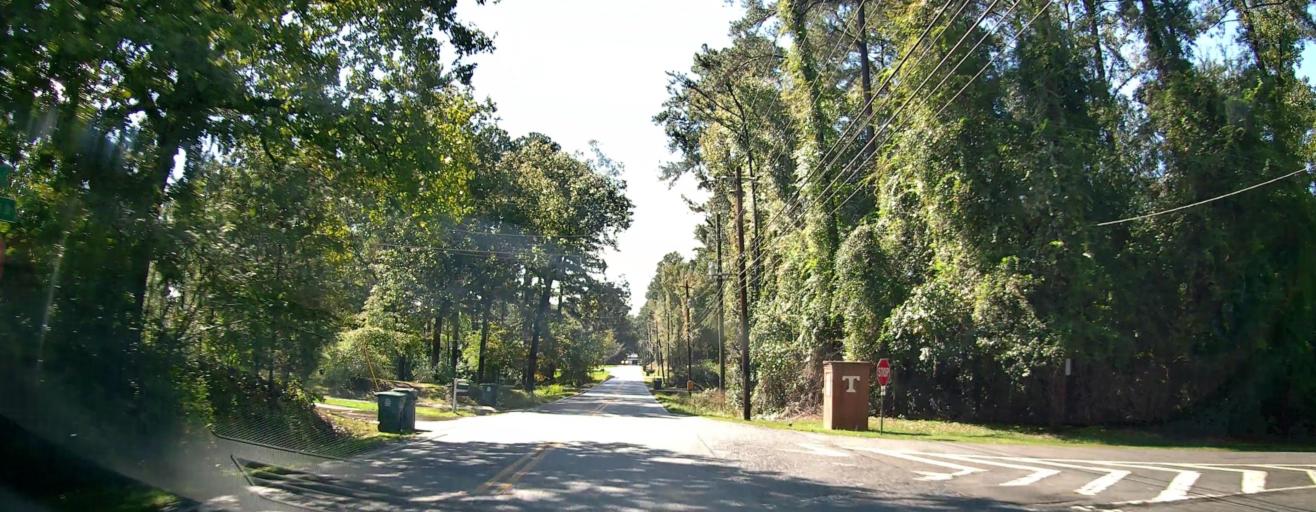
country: US
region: Georgia
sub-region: Bibb County
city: Macon
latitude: 32.8916
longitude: -83.7174
